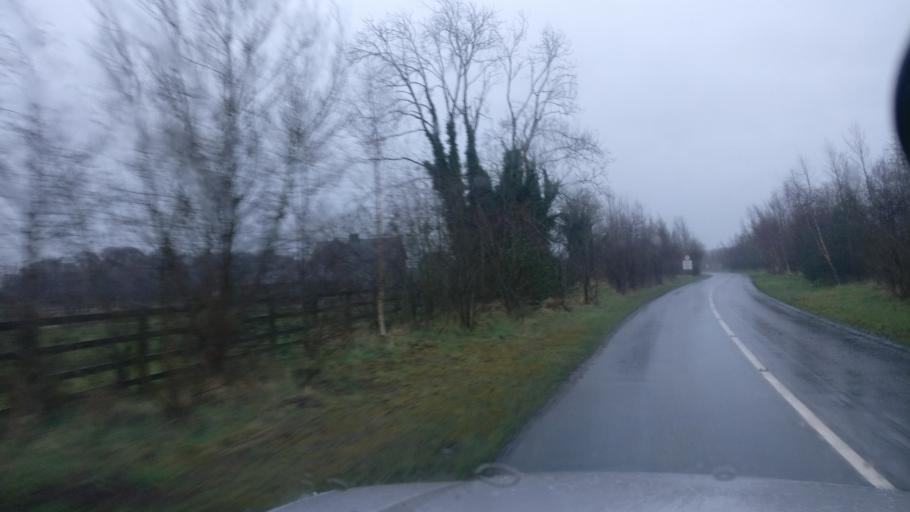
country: IE
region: Connaught
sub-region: County Galway
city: Ballinasloe
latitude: 53.3068
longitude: -8.3351
